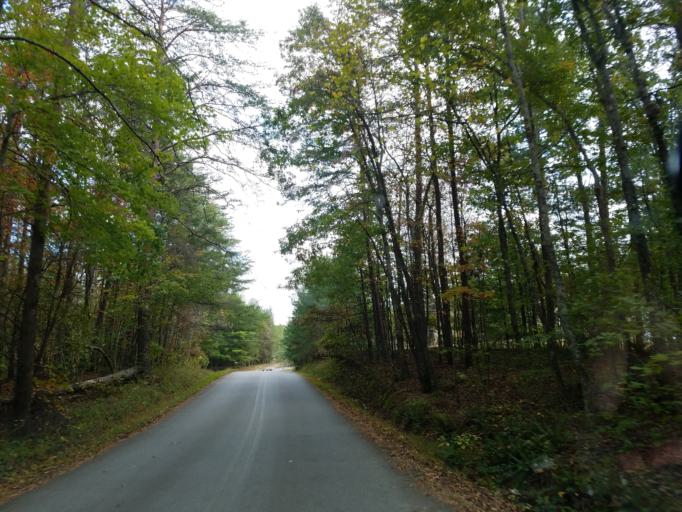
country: US
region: Georgia
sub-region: Gilmer County
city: Ellijay
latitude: 34.6242
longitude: -84.2856
